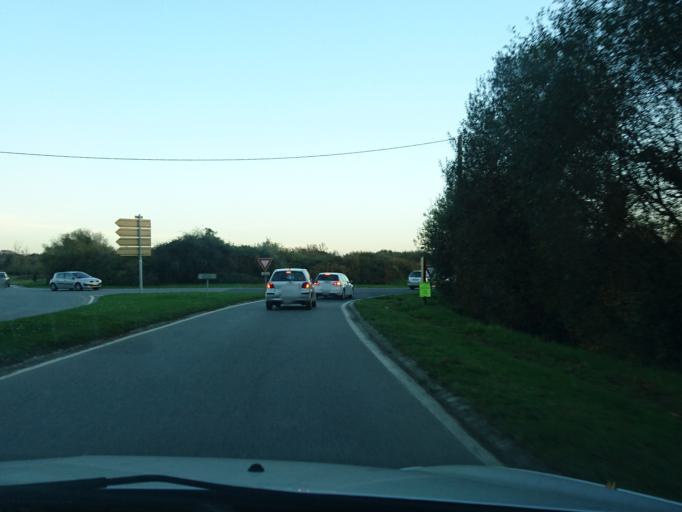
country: FR
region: Brittany
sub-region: Departement du Finistere
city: Saint-Renan
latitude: 48.4287
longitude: -4.6000
